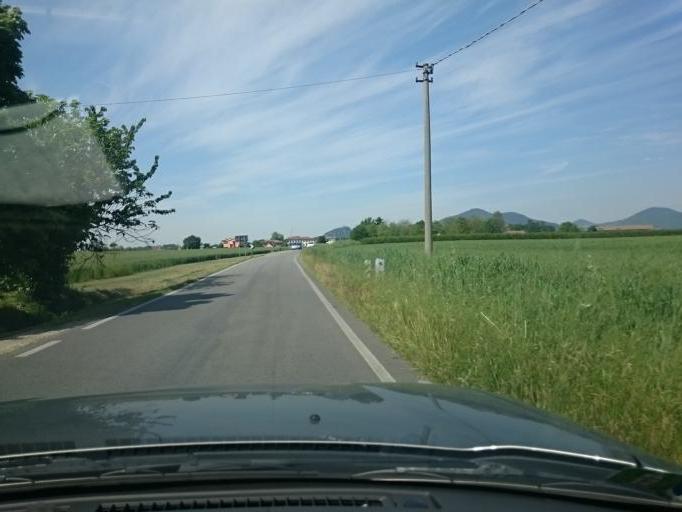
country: IT
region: Veneto
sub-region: Provincia di Padova
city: San Pietro Viminario
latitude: 45.2424
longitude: 11.8091
